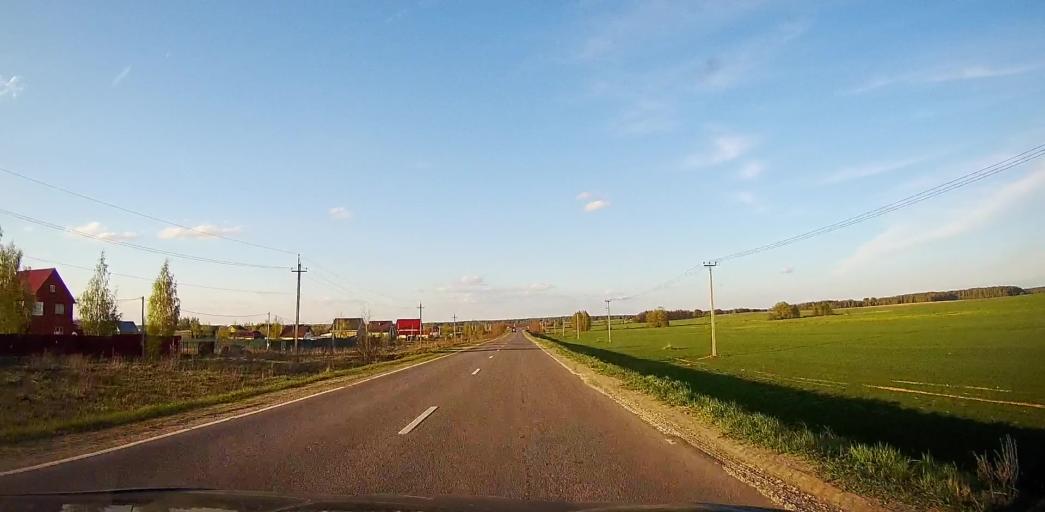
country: RU
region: Moskovskaya
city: Malino
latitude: 55.2782
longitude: 38.1693
